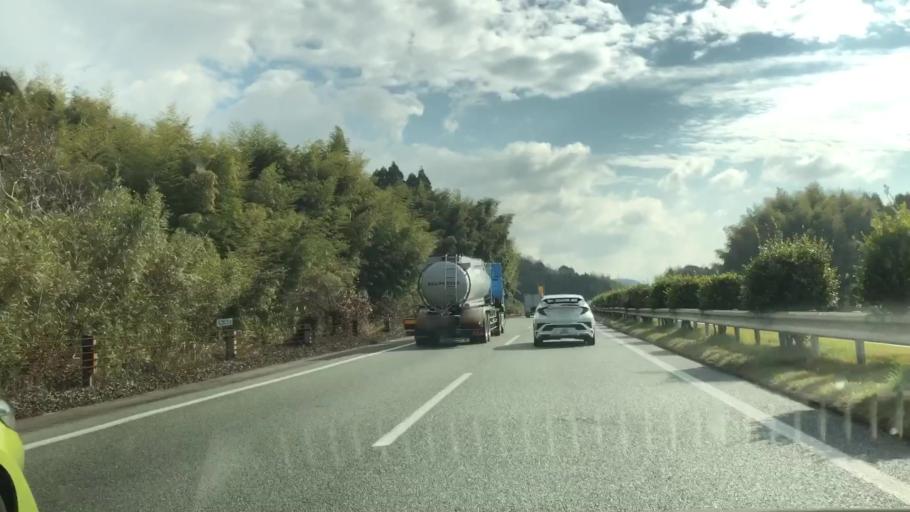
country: JP
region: Fukuoka
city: Setakamachi-takayanagi
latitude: 33.1092
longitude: 130.5328
